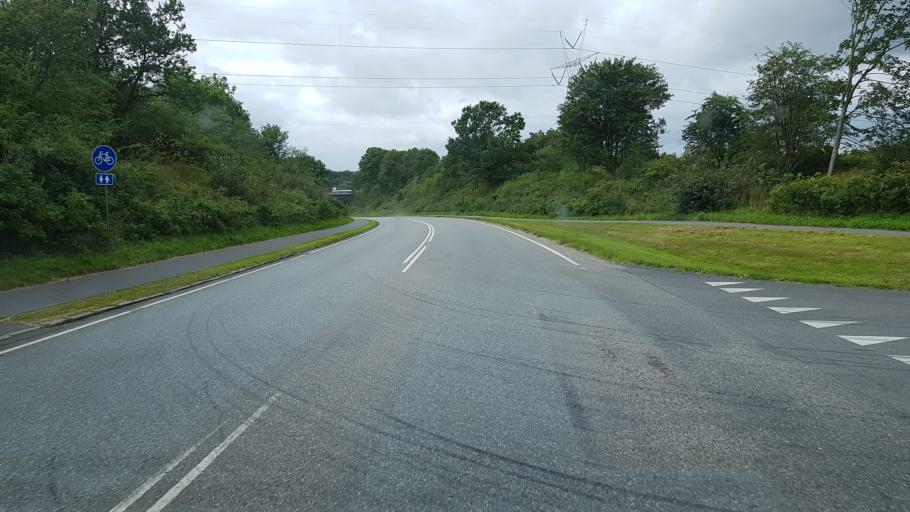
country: DK
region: South Denmark
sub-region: Kolding Kommune
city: Kolding
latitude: 55.4826
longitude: 9.4301
